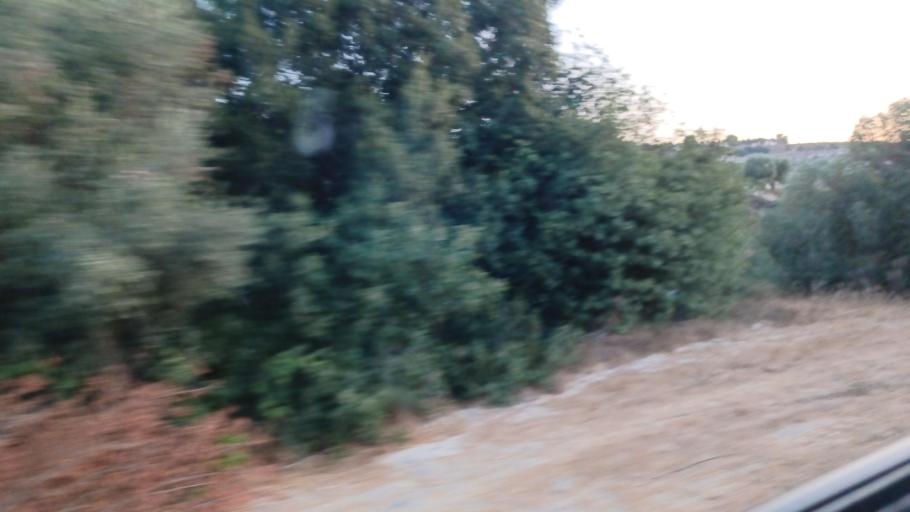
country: CY
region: Pafos
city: Mesogi
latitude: 34.8742
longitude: 32.5241
